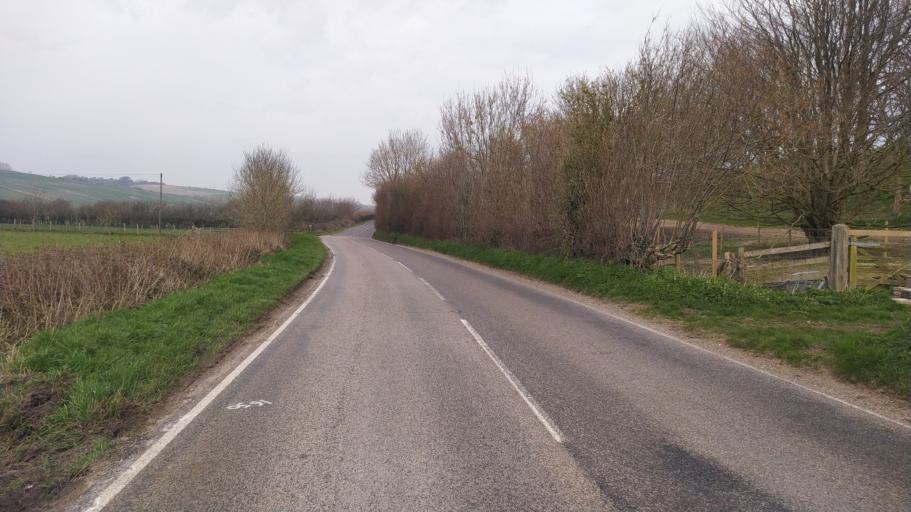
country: GB
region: England
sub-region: Dorset
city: Dorchester
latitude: 50.7625
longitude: -2.5537
